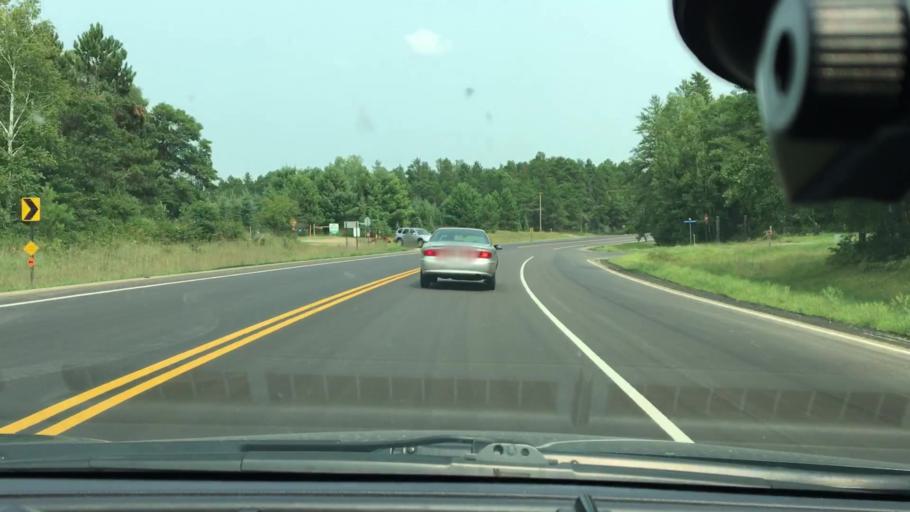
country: US
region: Minnesota
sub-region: Crow Wing County
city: Nisswa
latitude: 46.5282
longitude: -94.2668
